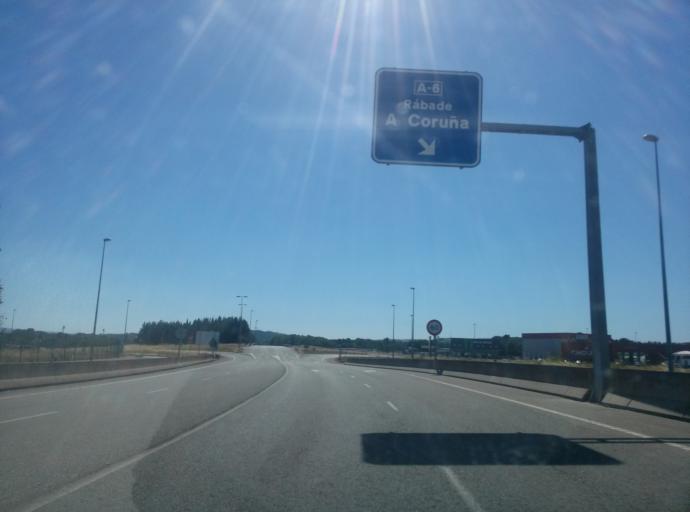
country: ES
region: Galicia
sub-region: Provincia de Lugo
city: Outeiro de Rei
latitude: 43.1077
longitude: -7.6008
